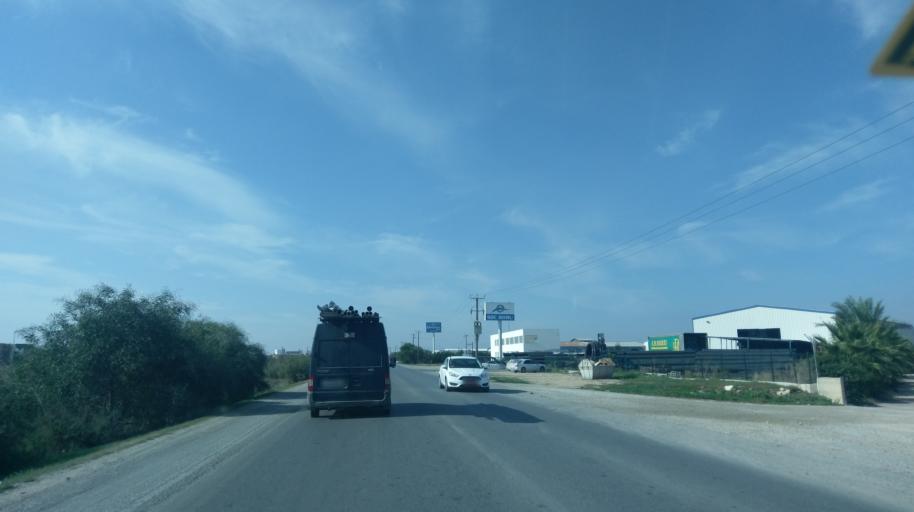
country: CY
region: Ammochostos
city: Famagusta
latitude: 35.1456
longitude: 33.8910
